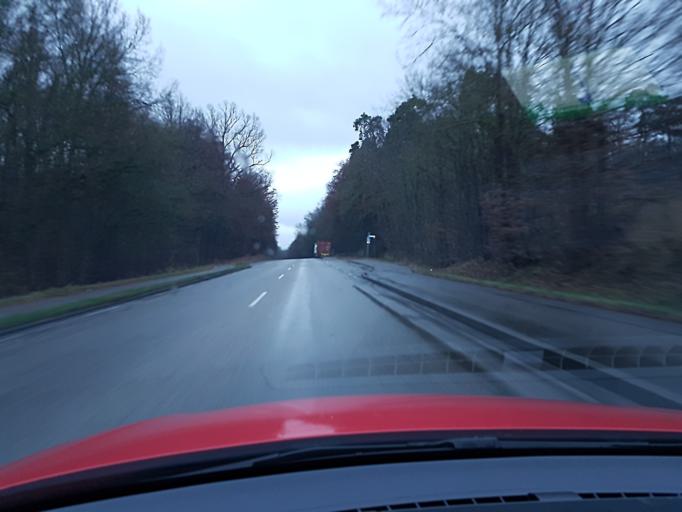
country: DE
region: Baden-Wuerttemberg
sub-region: Karlsruhe Region
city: Muhlacker
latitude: 48.9675
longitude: 8.8604
